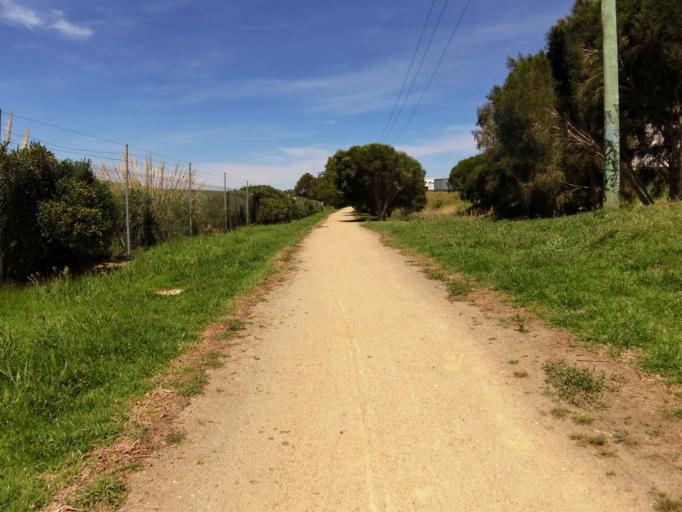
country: AU
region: Victoria
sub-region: Monash
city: Oakleigh South
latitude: -37.9464
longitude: 145.0872
